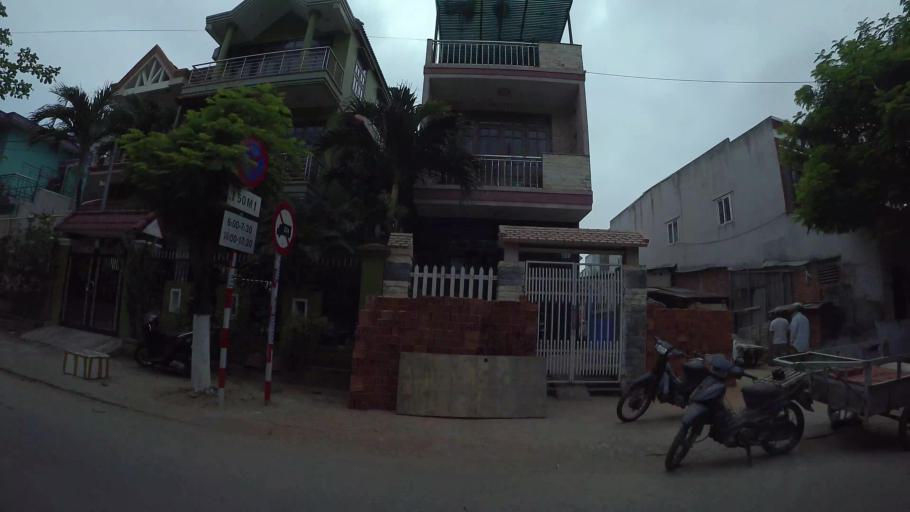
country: VN
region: Da Nang
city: Son Tra
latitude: 16.1003
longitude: 108.2541
